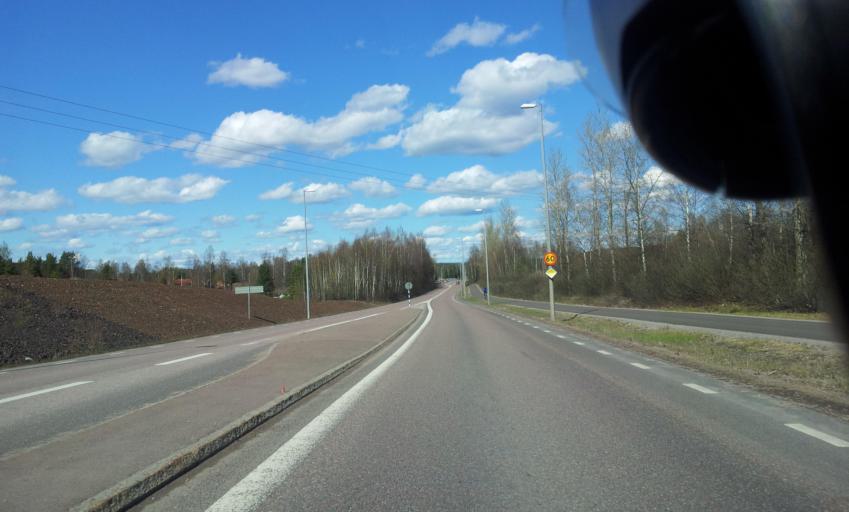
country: SE
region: Dalarna
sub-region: Faluns Kommun
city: Falun
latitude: 60.6119
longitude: 15.6162
